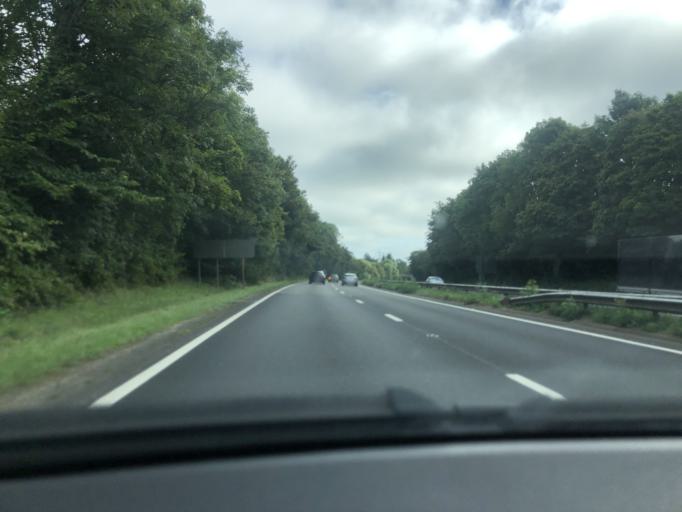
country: GB
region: England
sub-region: Devon
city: Honiton
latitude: 50.8001
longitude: -3.2030
